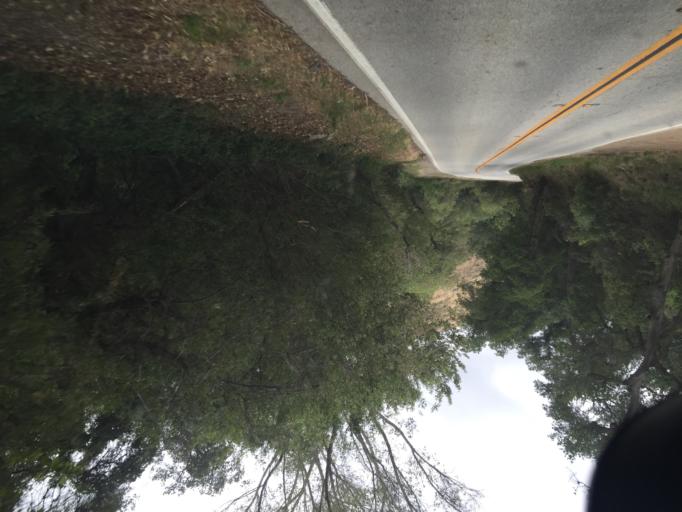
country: US
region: California
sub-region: Los Angeles County
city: Green Valley
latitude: 34.5531
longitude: -118.4241
